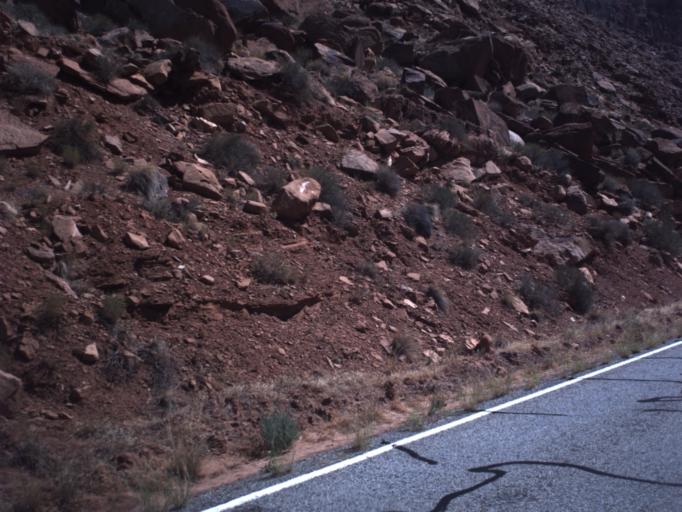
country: US
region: Utah
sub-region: Grand County
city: Moab
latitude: 38.7928
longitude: -109.3369
